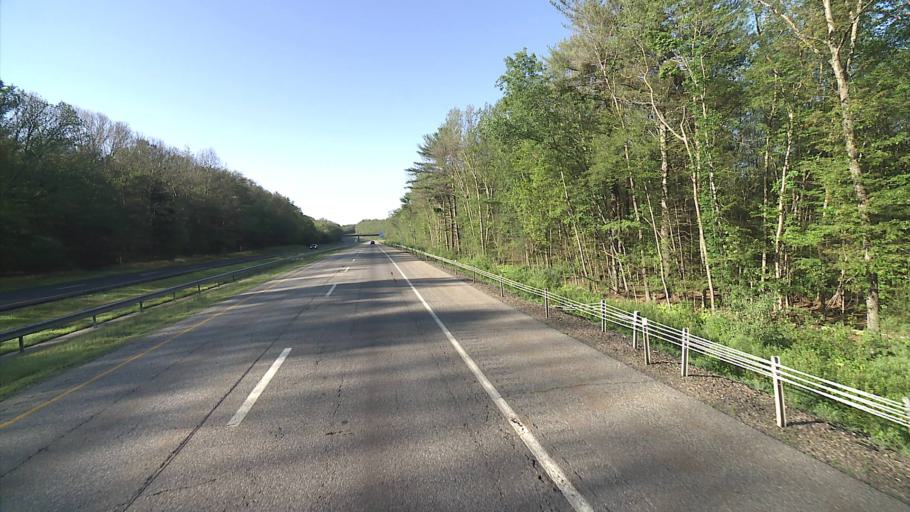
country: US
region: Connecticut
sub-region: Windham County
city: Danielson
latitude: 41.7748
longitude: -71.8723
